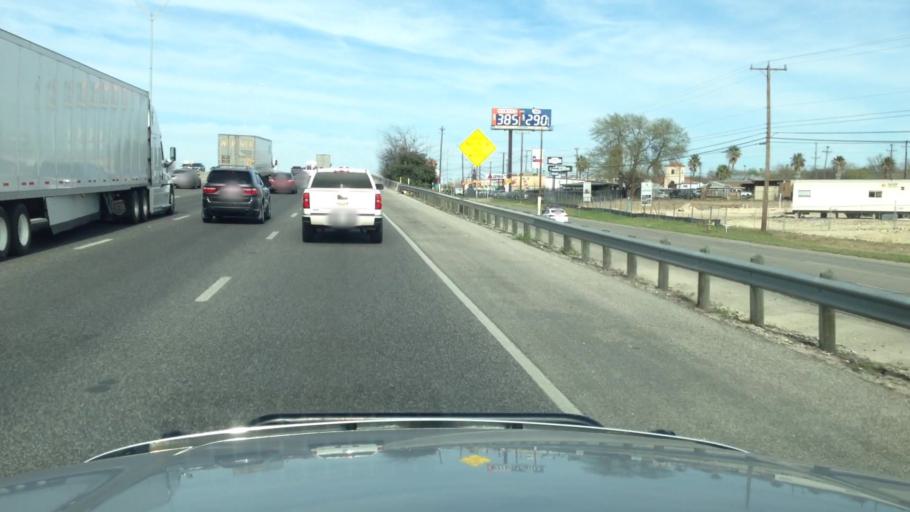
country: US
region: Texas
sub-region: Bexar County
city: Windcrest
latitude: 29.5379
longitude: -98.3820
